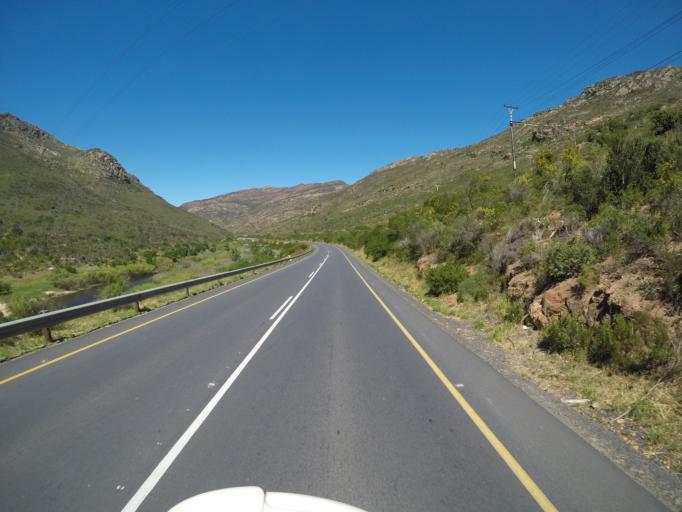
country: ZA
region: Western Cape
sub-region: Cape Winelands District Municipality
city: Ceres
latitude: -33.3068
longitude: 19.0698
